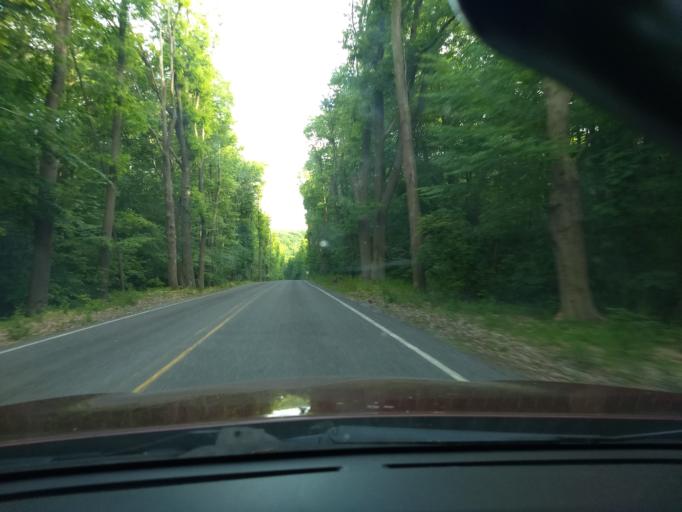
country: US
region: Pennsylvania
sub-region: Cambria County
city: Gallitzin
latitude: 40.5073
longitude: -78.5236
